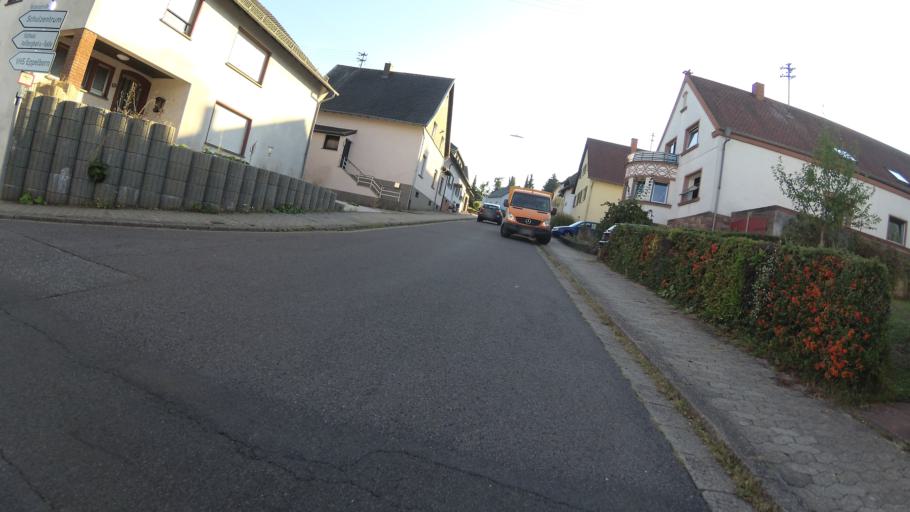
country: DE
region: Saarland
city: Eppelborn
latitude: 49.4044
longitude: 6.9567
